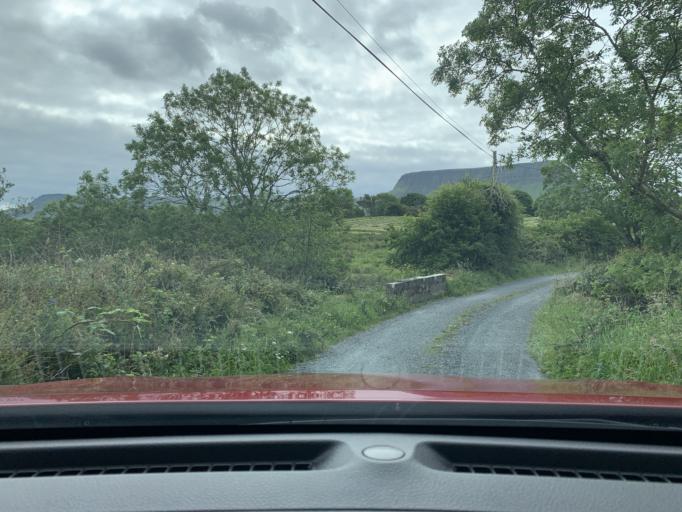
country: IE
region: Connaught
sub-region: Sligo
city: Sligo
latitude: 54.3824
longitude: -8.5226
